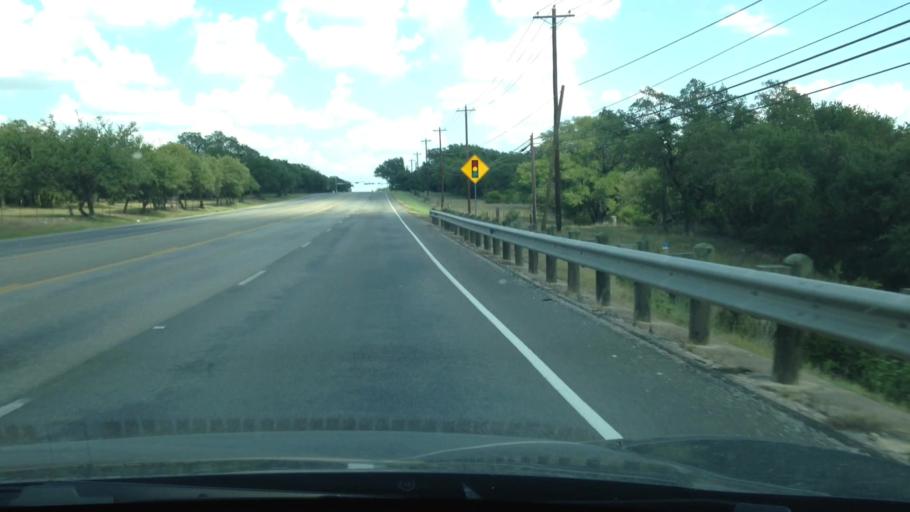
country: US
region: Texas
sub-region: Williamson County
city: Georgetown
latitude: 30.6332
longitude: -97.7696
